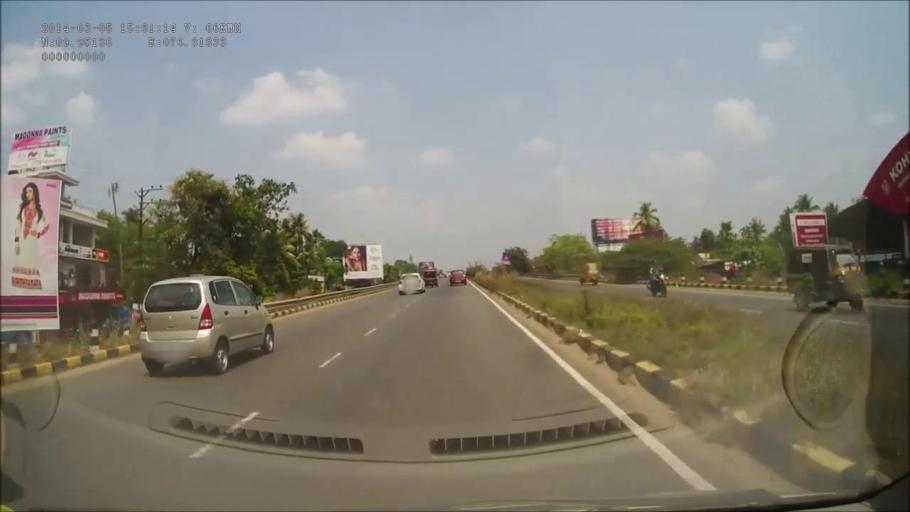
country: IN
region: Kerala
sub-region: Ernakulam
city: Cochin
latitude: 9.9519
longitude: 76.3183
